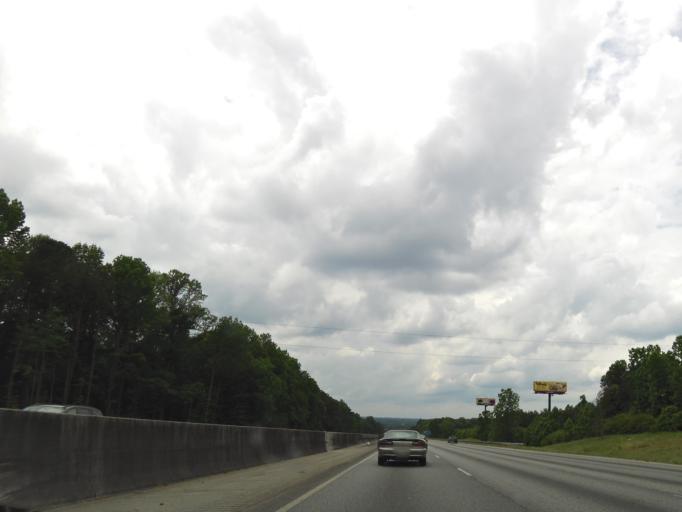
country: US
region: Georgia
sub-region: Cobb County
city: Mableton
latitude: 33.7758
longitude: -84.5888
